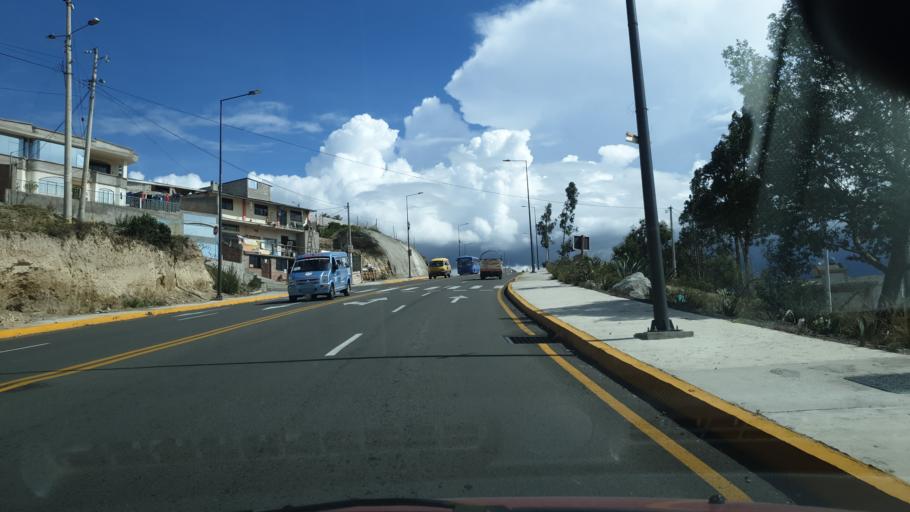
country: EC
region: Tungurahua
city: Ambato
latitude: -1.2925
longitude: -78.6302
